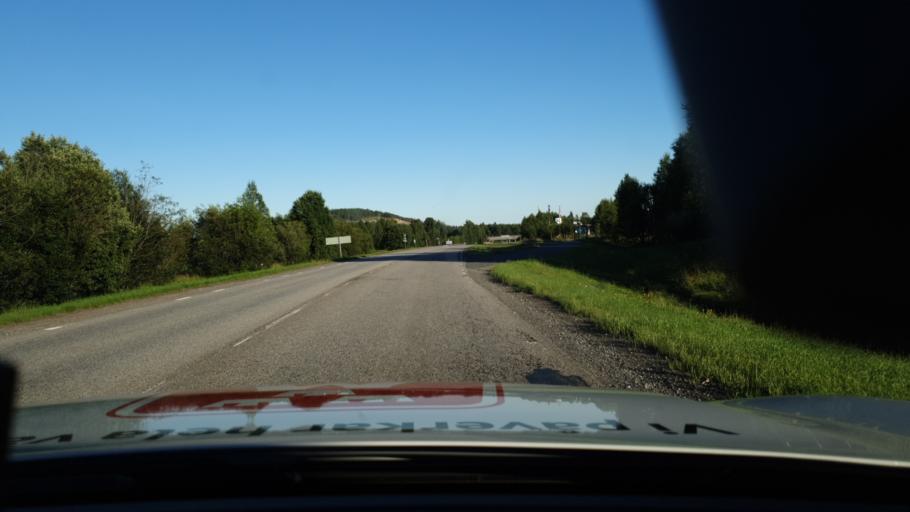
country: SE
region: Norrbotten
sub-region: Lulea Kommun
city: Sodra Sunderbyn
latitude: 65.5527
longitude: 21.8409
